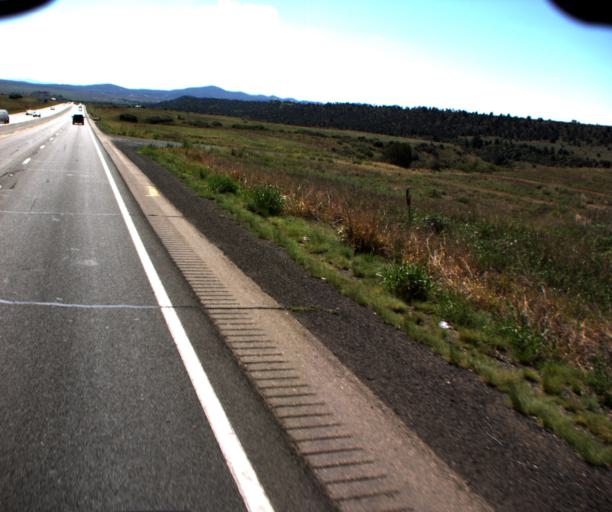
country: US
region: Arizona
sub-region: Yavapai County
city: Prescott Valley
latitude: 34.5788
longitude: -112.2960
